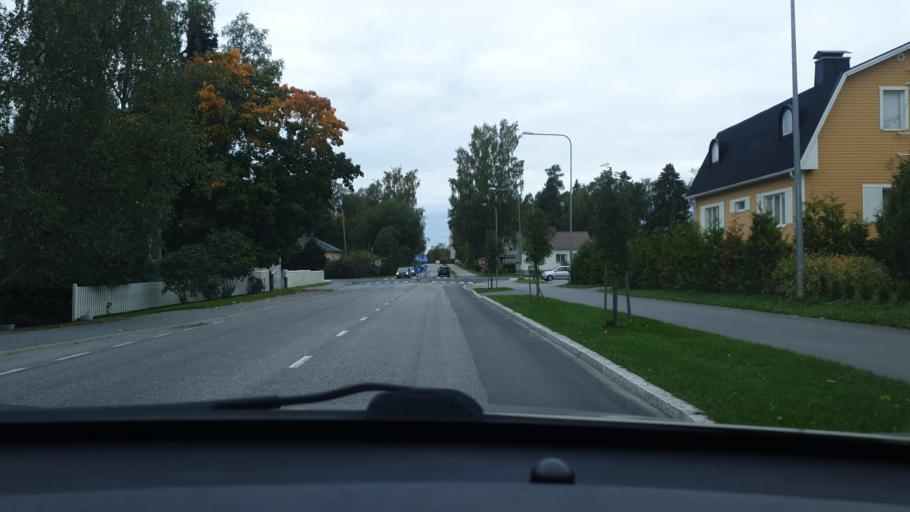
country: FI
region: Ostrobothnia
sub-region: Vaasa
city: Korsholm
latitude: 63.0947
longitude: 21.6683
